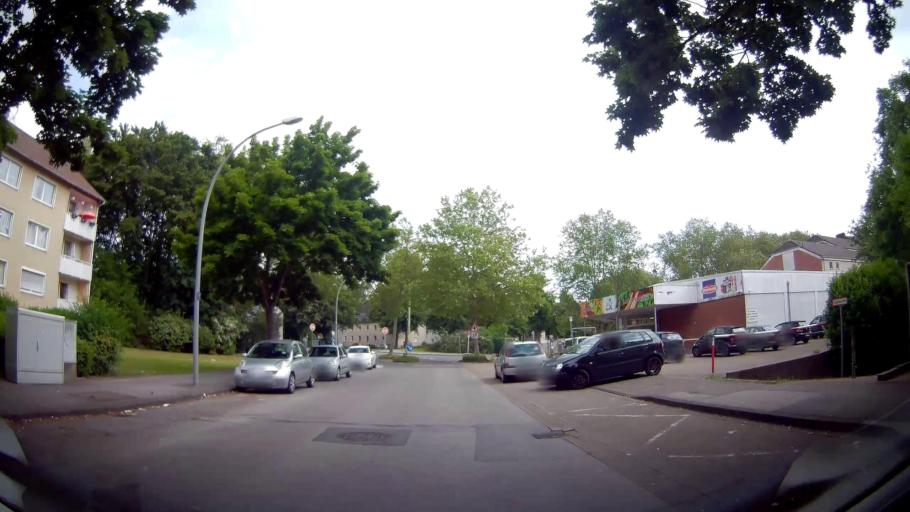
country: DE
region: North Rhine-Westphalia
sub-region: Regierungsbezirk Munster
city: Gladbeck
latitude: 51.5430
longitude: 7.0175
